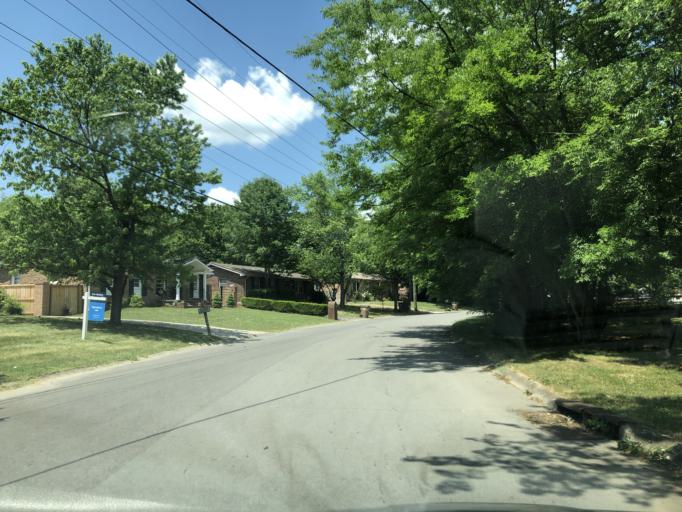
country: US
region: Tennessee
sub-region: Davidson County
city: Goodlettsville
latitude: 36.2697
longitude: -86.6951
